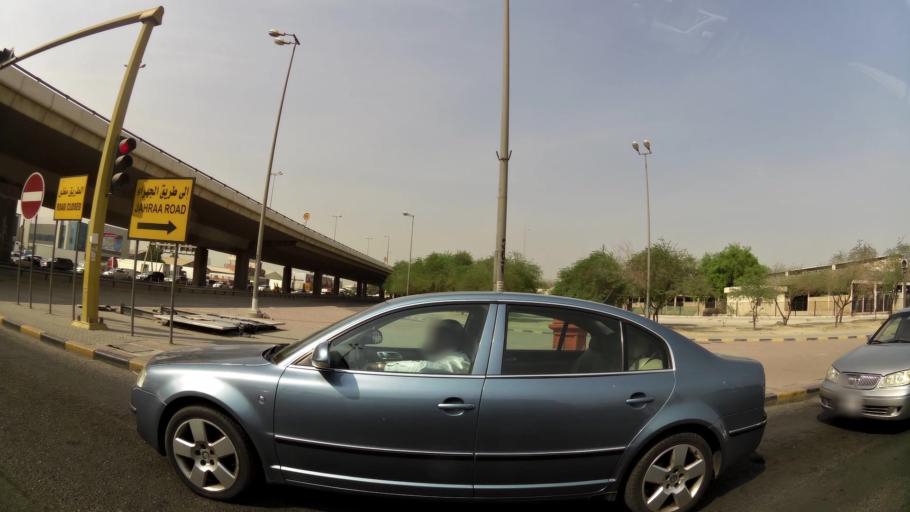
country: KW
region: Al Asimah
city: Ar Rabiyah
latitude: 29.3238
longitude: 47.9363
